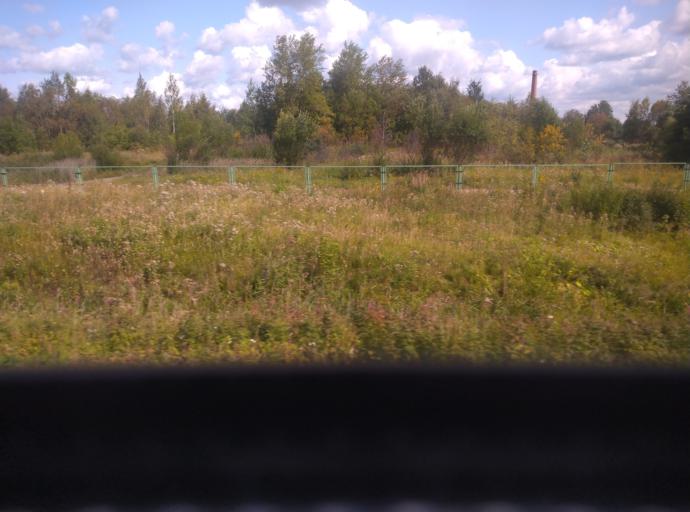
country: RU
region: St.-Petersburg
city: Kolpino
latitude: 59.7590
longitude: 30.5921
